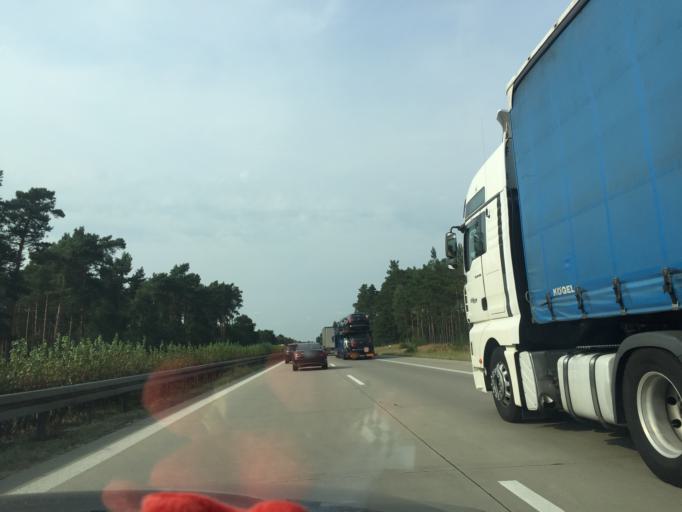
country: DE
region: Brandenburg
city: Halbe
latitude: 52.0680
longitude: 13.6519
